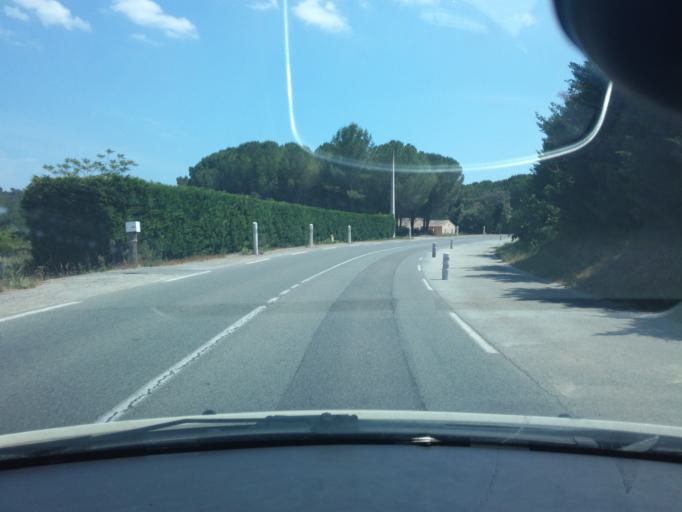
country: FR
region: Provence-Alpes-Cote d'Azur
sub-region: Departement du Var
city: Le Muy
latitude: 43.4866
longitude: 6.5672
